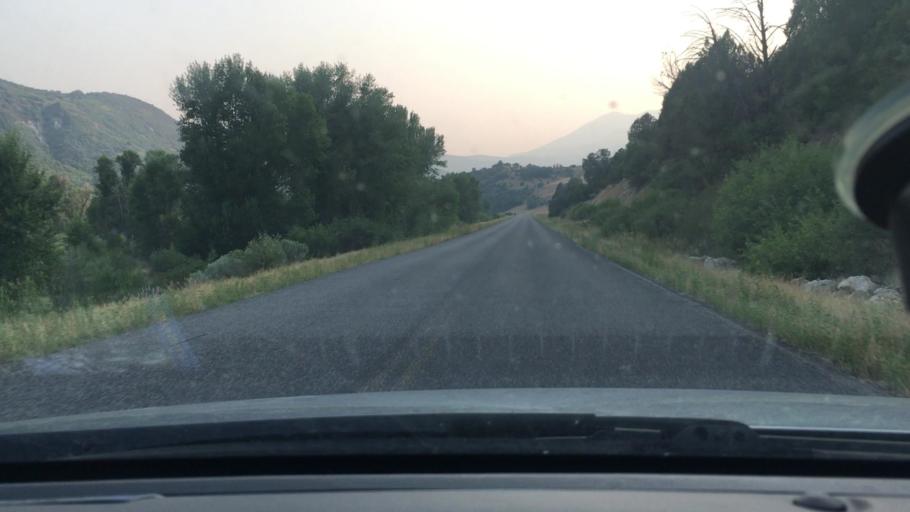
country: US
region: Utah
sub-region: Utah County
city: Mapleton
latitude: 40.0559
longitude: -111.4593
